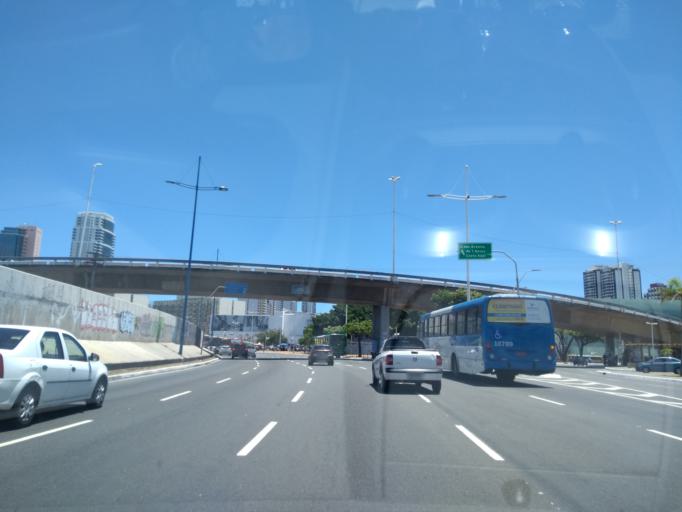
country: BR
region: Bahia
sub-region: Salvador
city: Salvador
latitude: -12.9800
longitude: -38.4671
